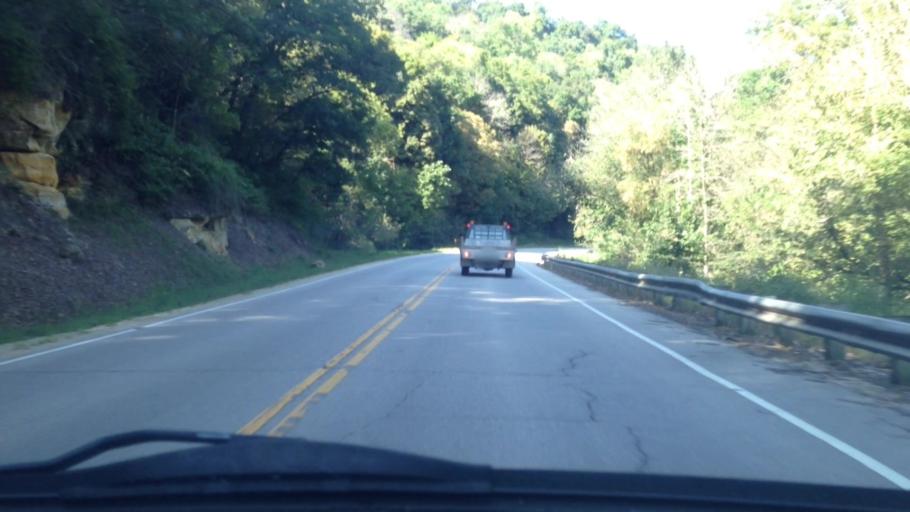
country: US
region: Minnesota
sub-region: Fillmore County
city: Rushford
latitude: 43.7607
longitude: -91.7656
